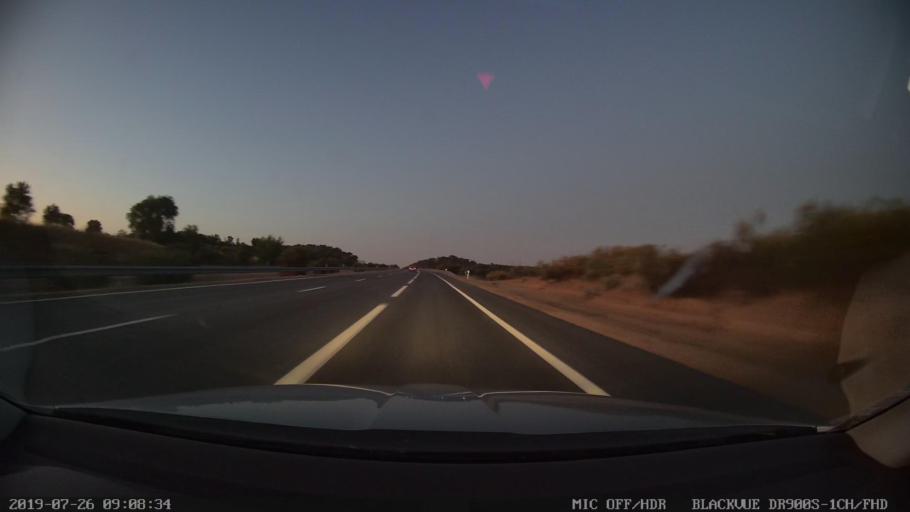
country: PT
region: Evora
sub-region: Estremoz
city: Estremoz
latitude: 38.7558
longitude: -7.7143
